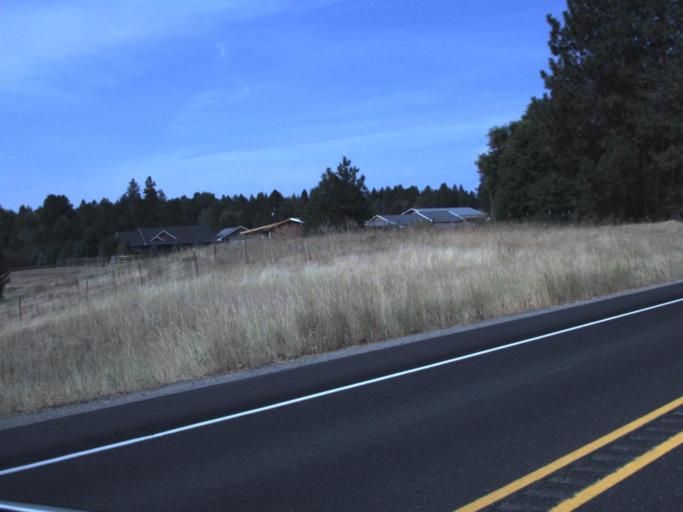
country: US
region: Washington
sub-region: Spokane County
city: Deer Park
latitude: 47.9155
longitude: -117.4511
